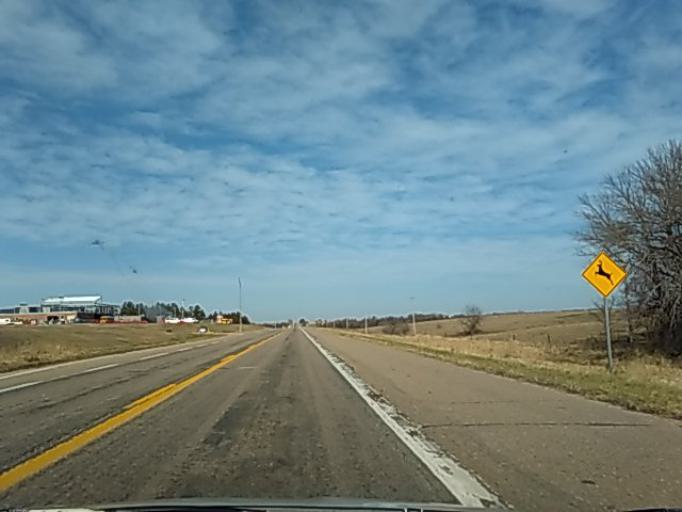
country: US
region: Nebraska
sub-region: Clay County
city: Clay Center
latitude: 40.4300
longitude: -98.0514
